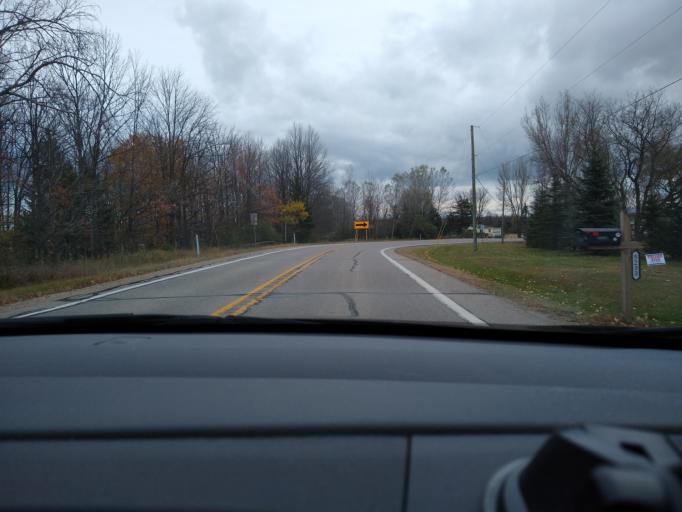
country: US
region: Michigan
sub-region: Delta County
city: Escanaba
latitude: 45.7380
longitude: -87.2647
